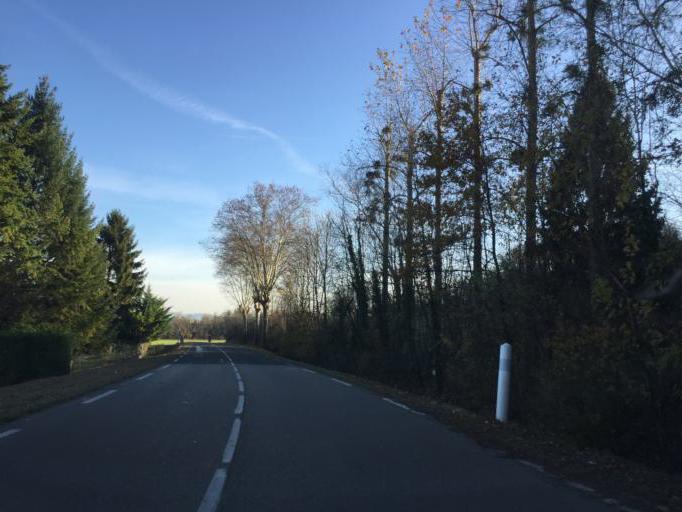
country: FR
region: Rhone-Alpes
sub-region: Departement de l'Ain
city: Chatillon-la-Palud
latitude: 45.9418
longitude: 5.2433
